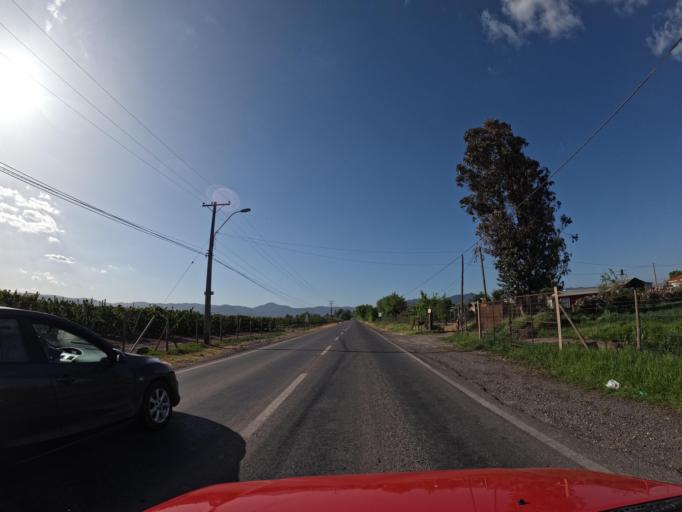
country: CL
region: Maule
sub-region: Provincia de Curico
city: Rauco
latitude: -34.8966
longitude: -71.2736
